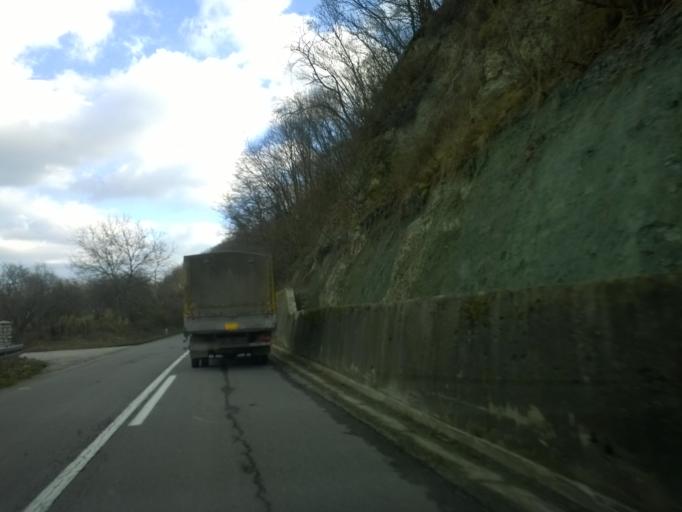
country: RO
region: Caras-Severin
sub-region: Comuna Berzasca
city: Liubcova
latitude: 44.6469
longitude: 21.8533
